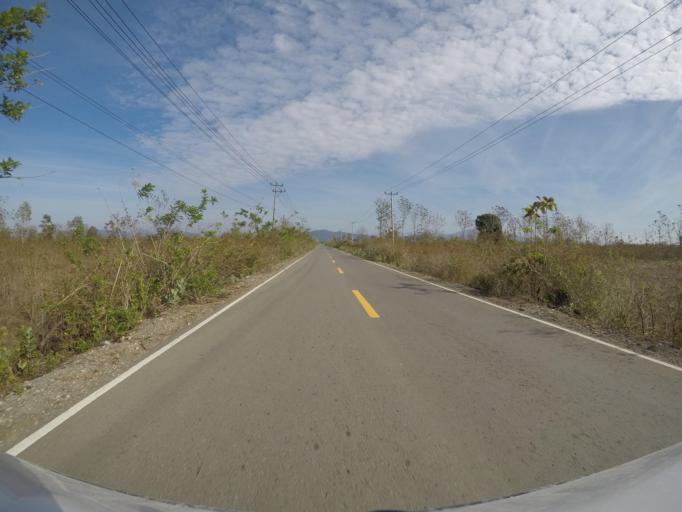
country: TL
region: Bobonaro
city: Maliana
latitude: -8.9406
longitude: 125.1999
